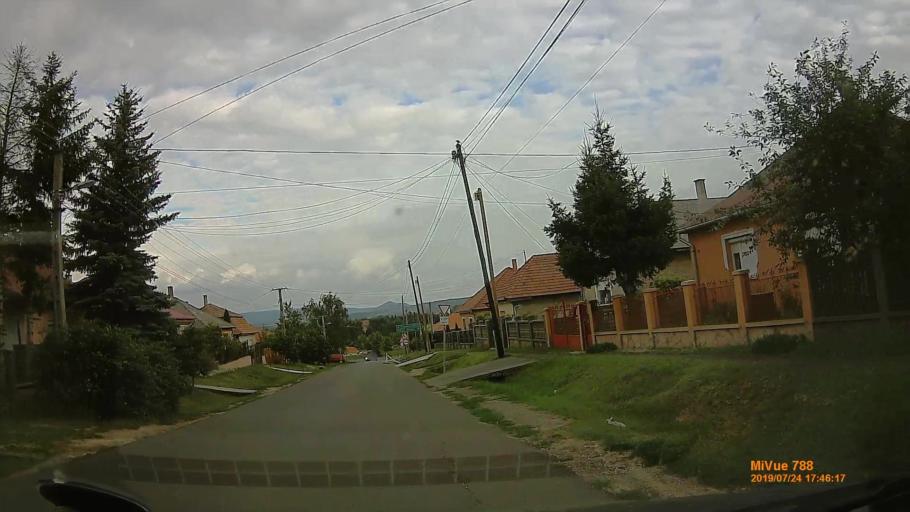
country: HU
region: Borsod-Abauj-Zemplen
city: Encs
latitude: 48.3375
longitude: 21.1062
